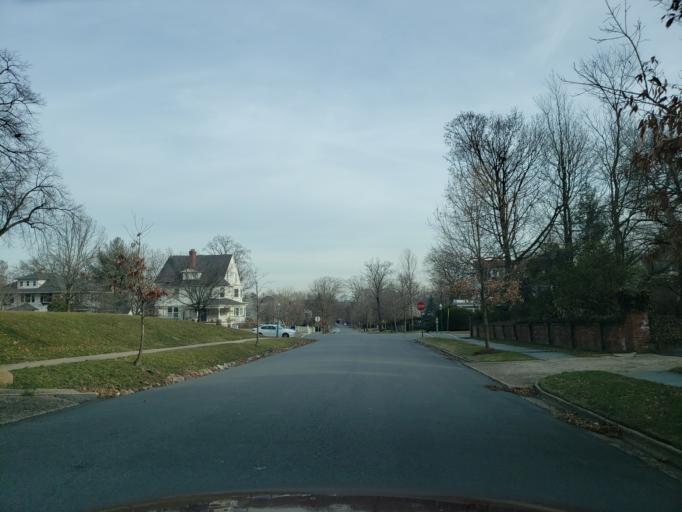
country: US
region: New Jersey
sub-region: Essex County
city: Glen Ridge
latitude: 40.7939
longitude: -74.2124
